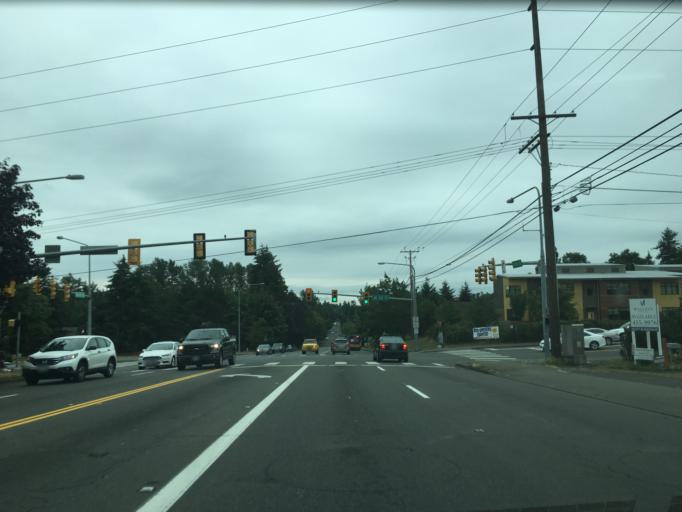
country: US
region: Washington
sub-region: King County
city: Inglewood-Finn Hill
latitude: 47.7189
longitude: -122.2078
